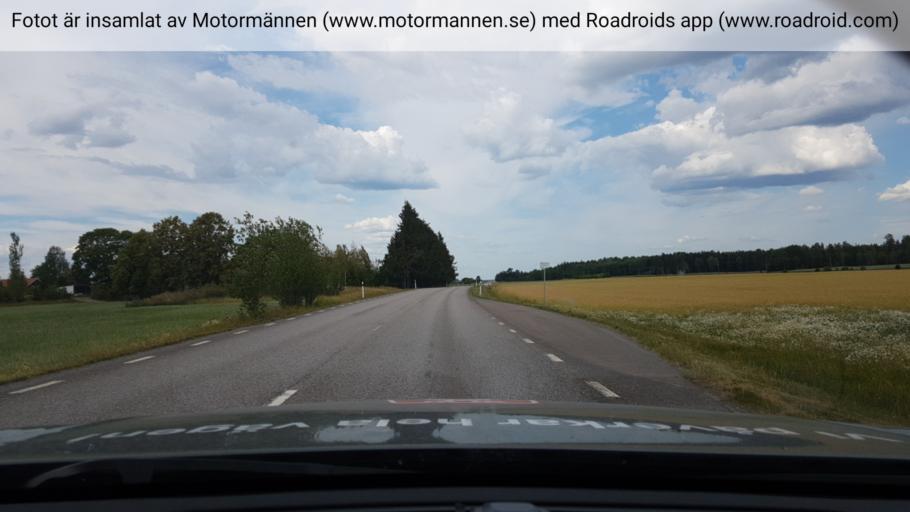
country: SE
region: Vaestmanland
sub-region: Sala Kommun
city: Sala
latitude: 59.8637
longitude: 16.6308
